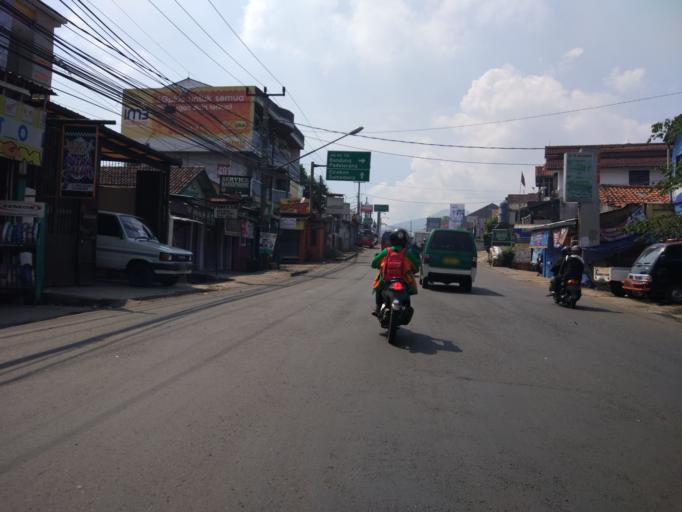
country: ID
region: West Java
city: Cileunyi
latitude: -6.9381
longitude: 107.7550
